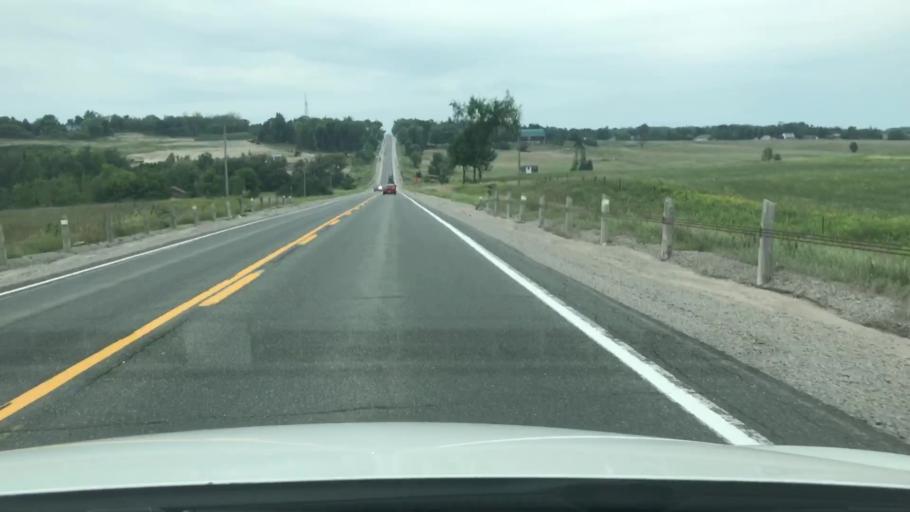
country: CA
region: Ontario
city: Innisfil
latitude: 44.2431
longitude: -79.5988
